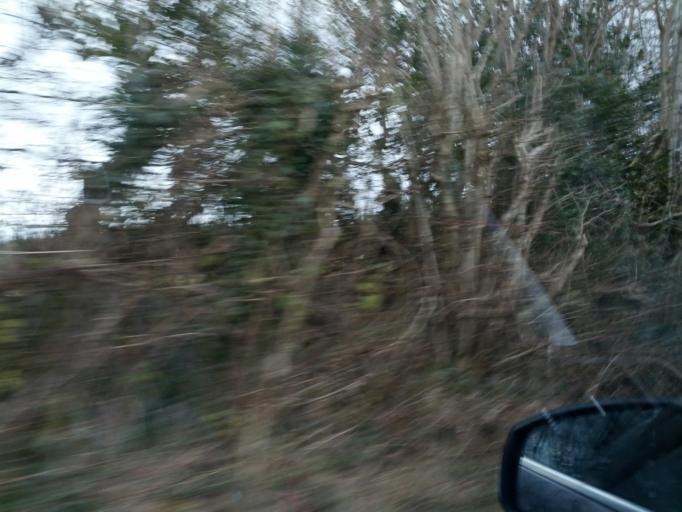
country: IE
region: Connaught
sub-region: County Galway
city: Athenry
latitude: 53.3548
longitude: -8.6568
